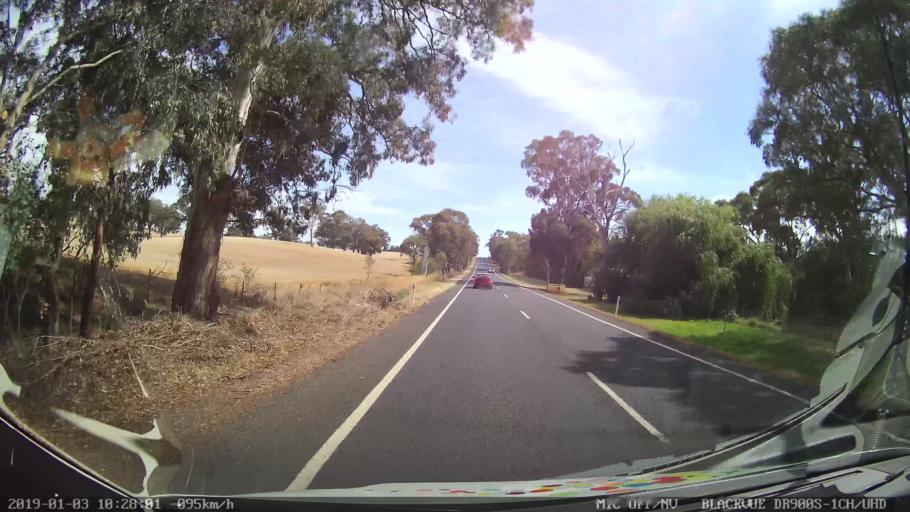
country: AU
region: New South Wales
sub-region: Young
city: Young
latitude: -34.3937
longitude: 148.2586
